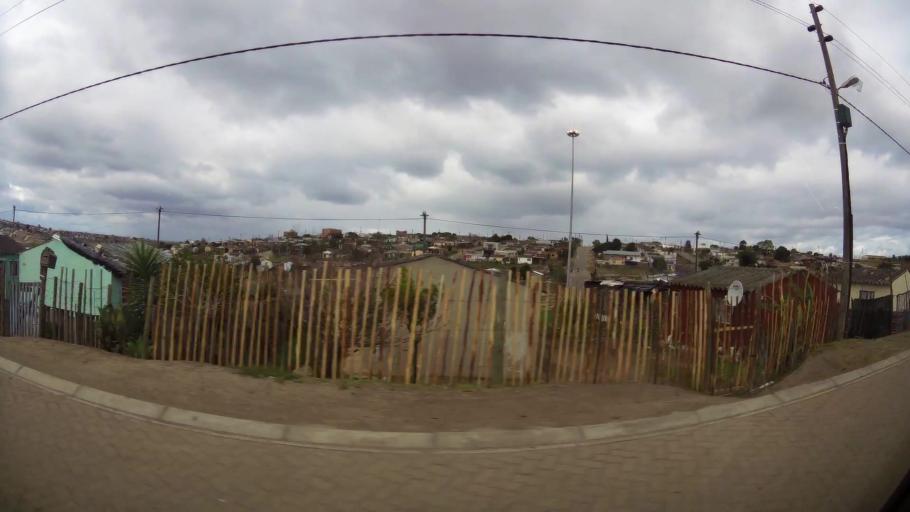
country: ZA
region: Western Cape
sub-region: Eden District Municipality
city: George
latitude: -34.0145
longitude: 22.4792
